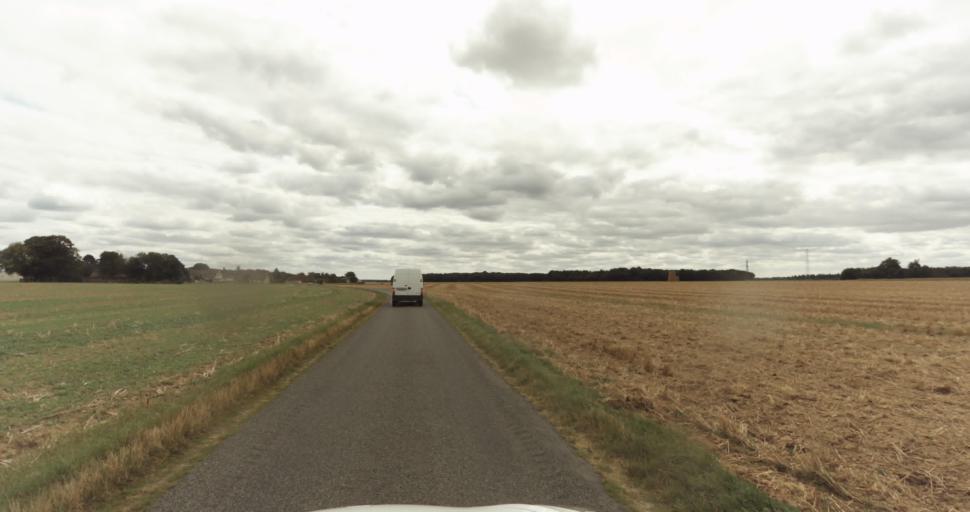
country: FR
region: Haute-Normandie
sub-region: Departement de l'Eure
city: Saint-Germain-sur-Avre
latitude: 48.8036
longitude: 1.2569
